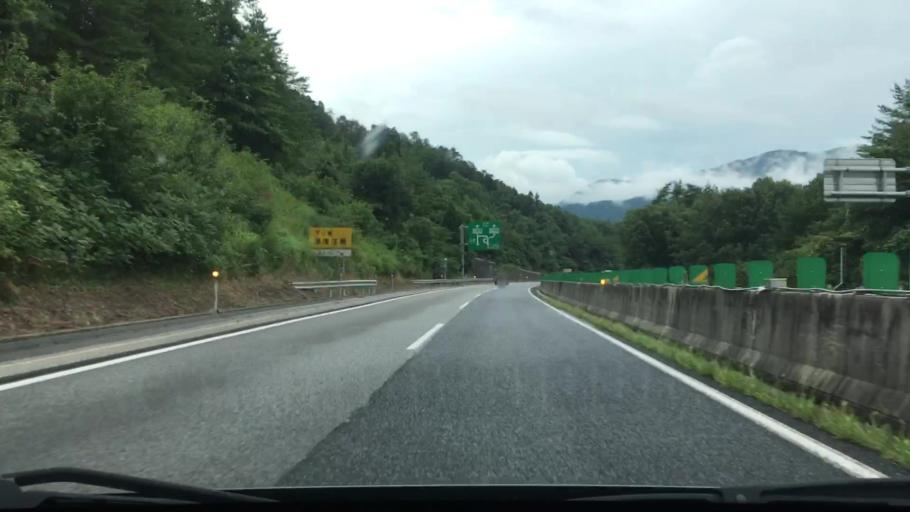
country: JP
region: Hiroshima
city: Hiroshima-shi
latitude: 34.5841
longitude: 132.4740
